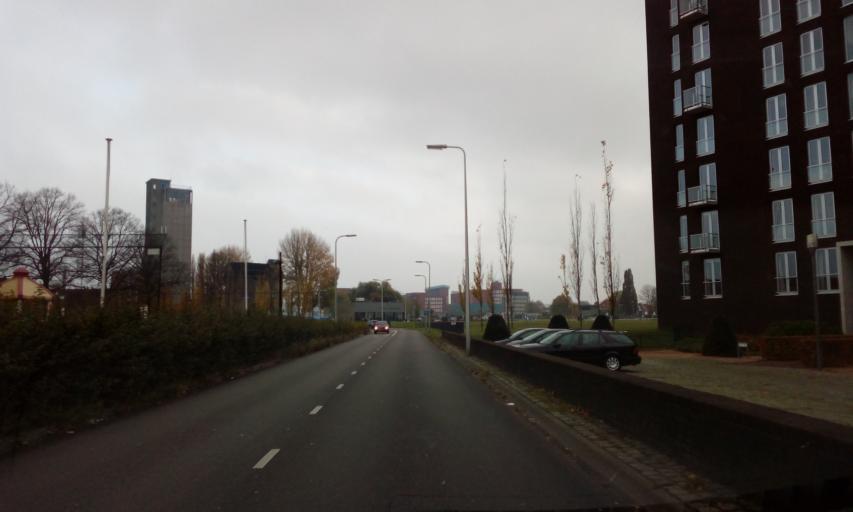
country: NL
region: Overijssel
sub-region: Gemeente Deventer
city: Deventer
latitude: 52.2469
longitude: 6.1656
